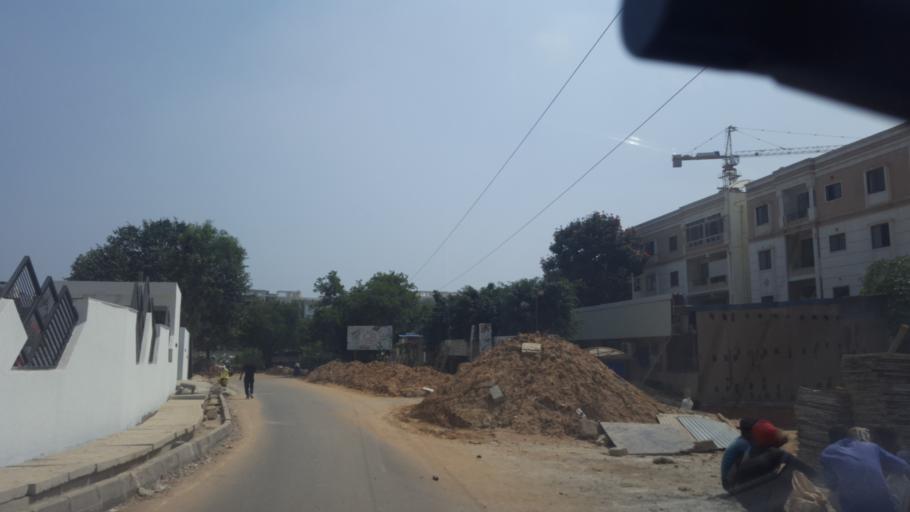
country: IN
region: Karnataka
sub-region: Bangalore Urban
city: Bangalore
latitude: 12.9430
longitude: 77.6984
